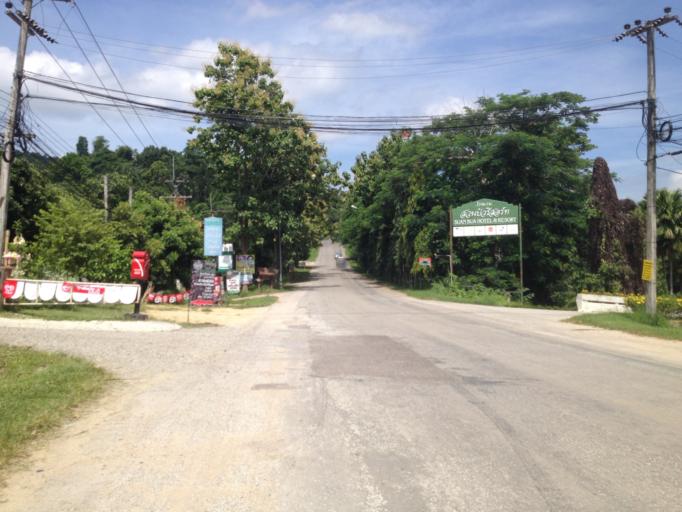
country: TH
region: Chiang Mai
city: Hang Dong
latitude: 18.7848
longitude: 98.8439
